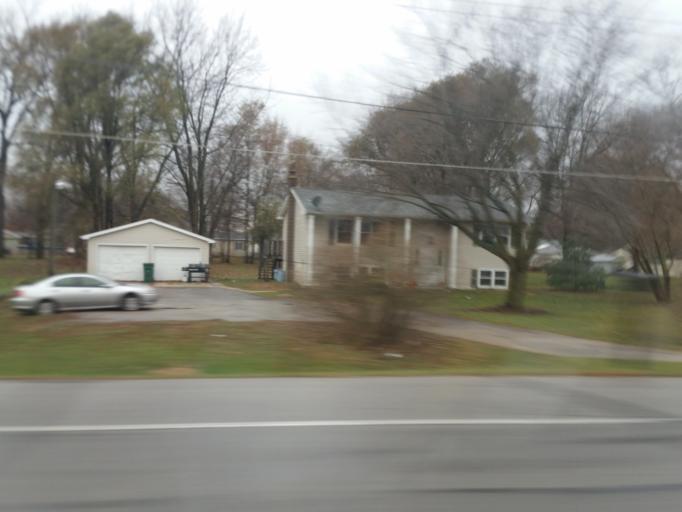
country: US
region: Iowa
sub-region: Black Hawk County
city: Elk Run Heights
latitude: 42.4074
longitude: -92.2631
